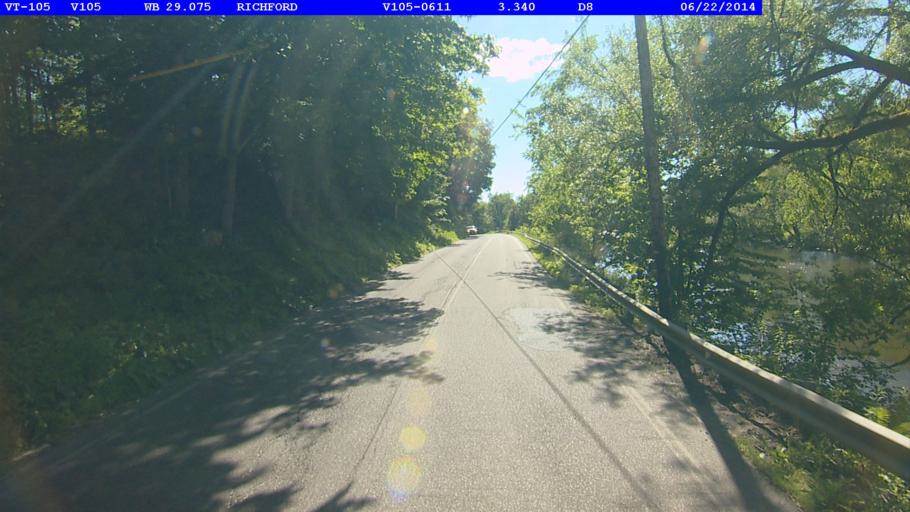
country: US
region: Vermont
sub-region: Franklin County
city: Richford
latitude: 44.9875
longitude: -72.6517
